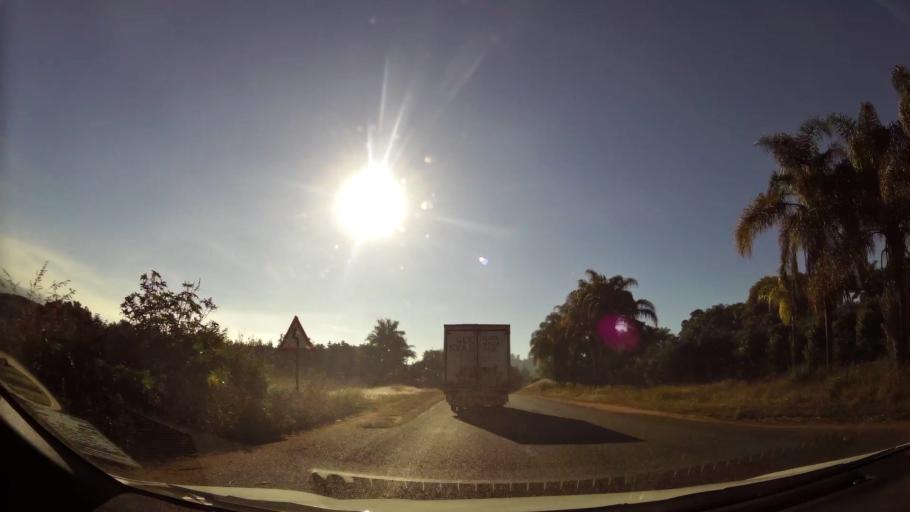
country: ZA
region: Limpopo
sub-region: Mopani District Municipality
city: Tzaneen
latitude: -23.8929
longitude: 30.0781
